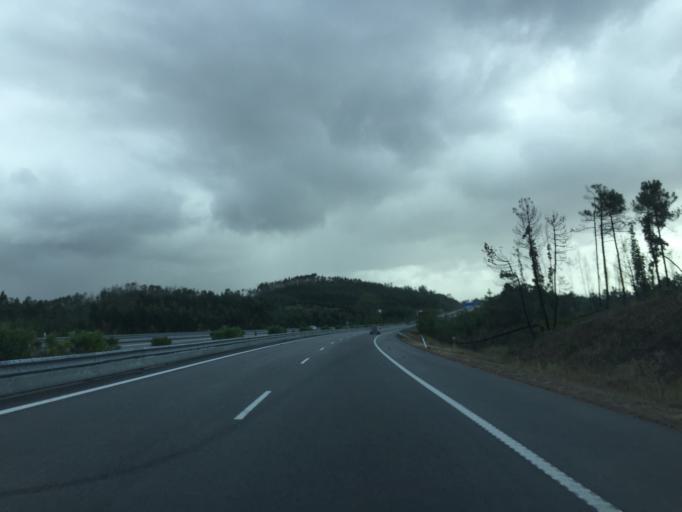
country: PT
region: Aveiro
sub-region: Mealhada
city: Pampilhosa do Botao
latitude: 40.2839
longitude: -8.5140
